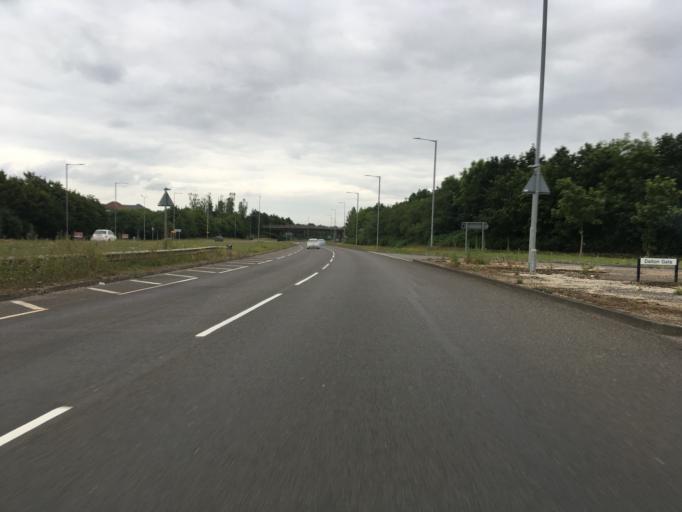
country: GB
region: England
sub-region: Milton Keynes
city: Broughton
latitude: 52.0472
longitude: -0.7045
